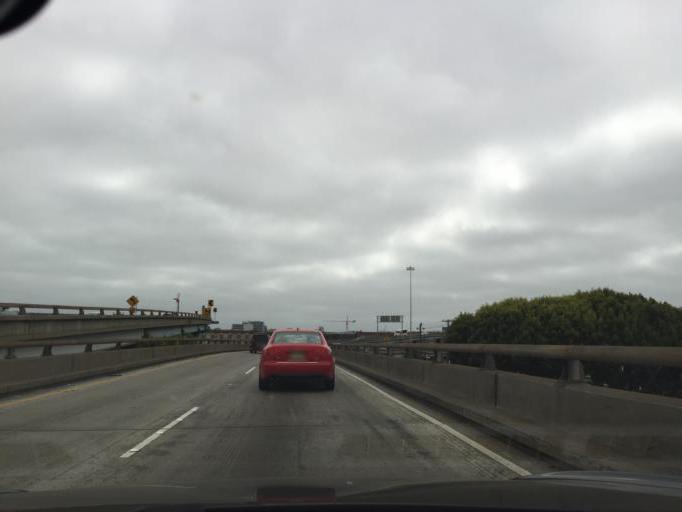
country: US
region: California
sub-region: San Francisco County
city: San Francisco
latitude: 37.7688
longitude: -122.4084
